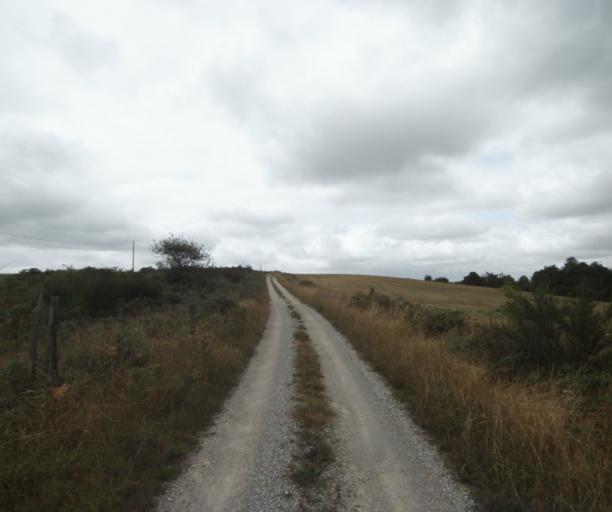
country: FR
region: Midi-Pyrenees
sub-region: Departement du Tarn
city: Soreze
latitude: 43.4322
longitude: 2.1098
